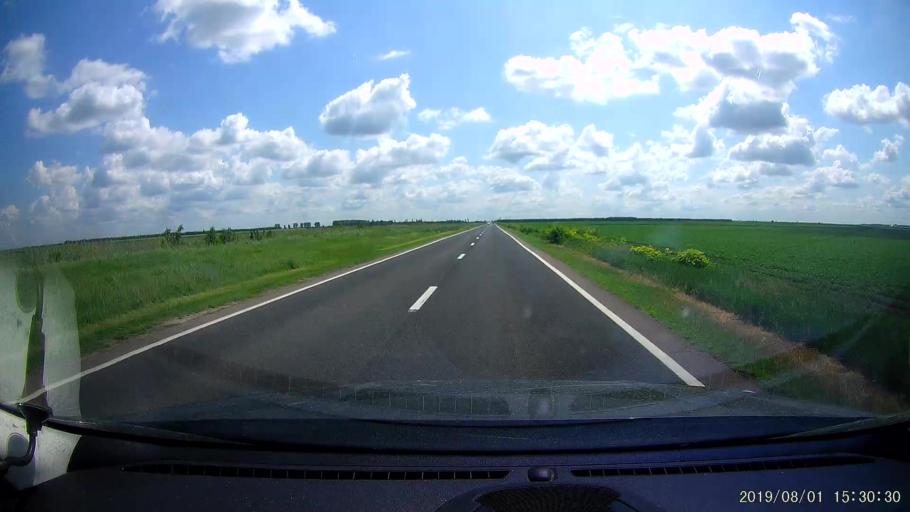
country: RO
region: Braila
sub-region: Comuna Viziru
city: Viziru
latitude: 44.9626
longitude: 27.6766
